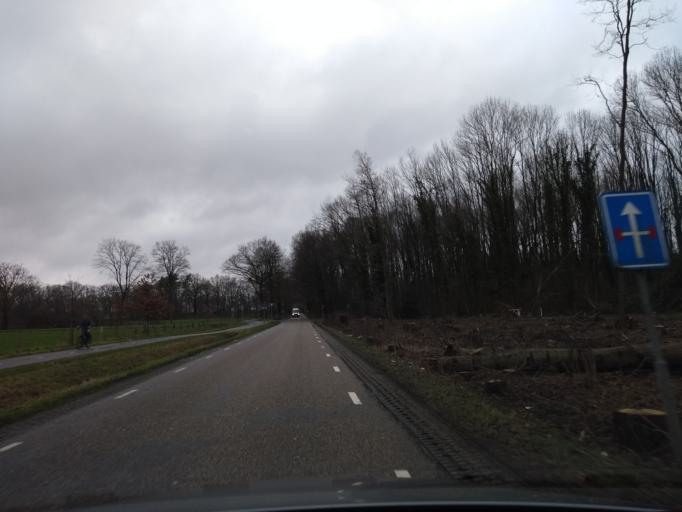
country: NL
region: Overijssel
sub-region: Gemeente Enschede
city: Enschede
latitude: 52.2105
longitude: 6.9305
